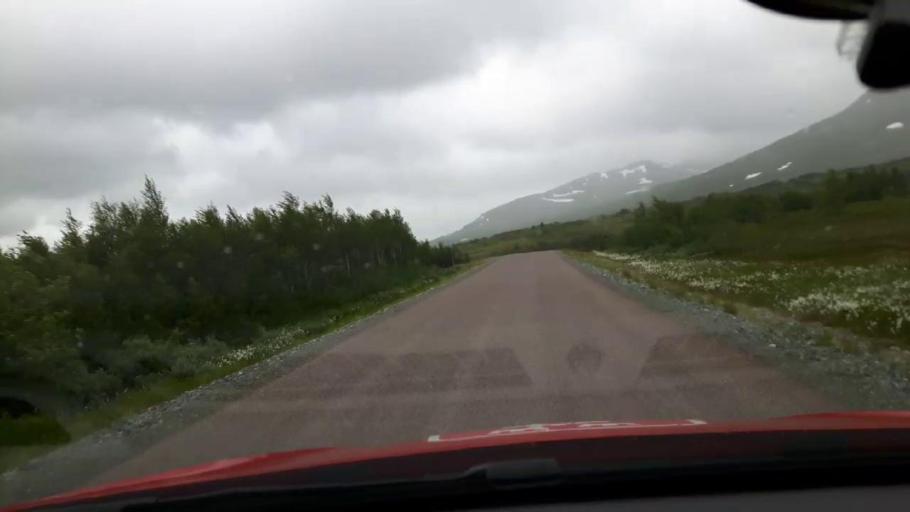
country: NO
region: Nord-Trondelag
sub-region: Meraker
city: Meraker
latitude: 63.2159
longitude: 12.4077
